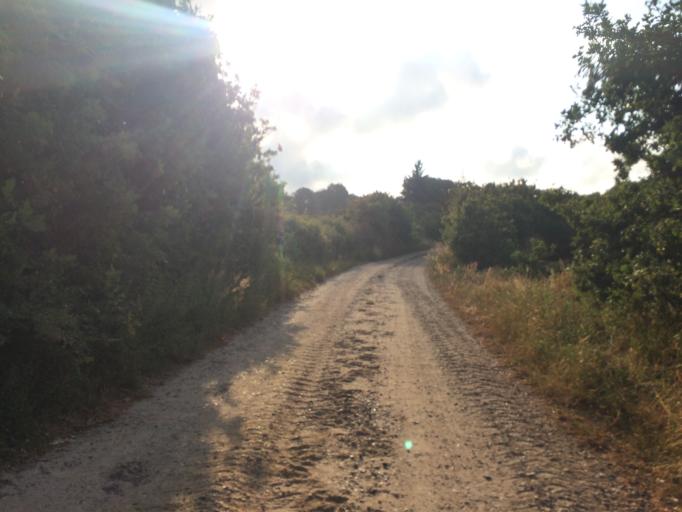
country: DK
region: Central Jutland
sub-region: Struer Kommune
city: Struer
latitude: 56.6076
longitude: 8.6947
